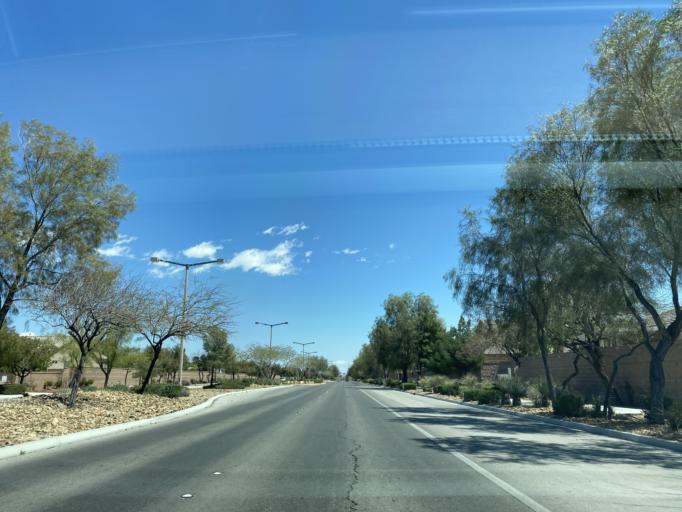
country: US
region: Nevada
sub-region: Clark County
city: North Las Vegas
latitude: 36.3050
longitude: -115.2210
